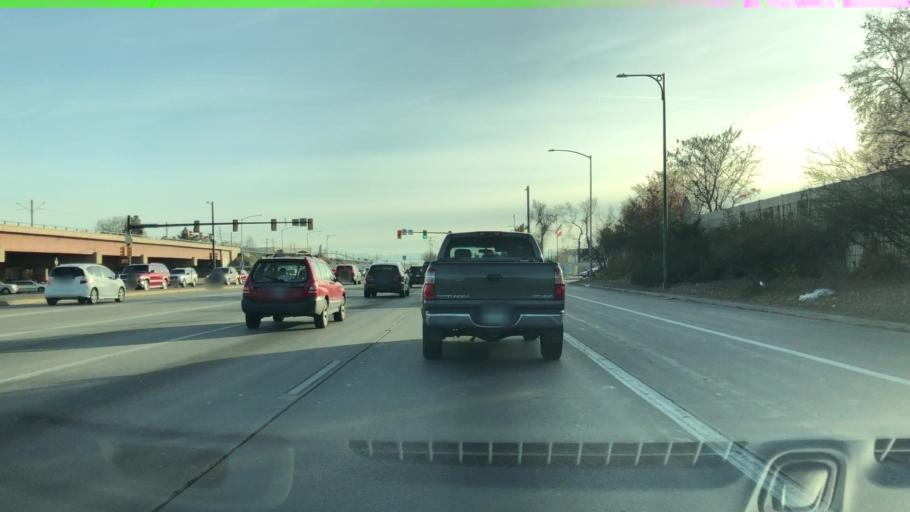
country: US
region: Colorado
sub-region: Arapahoe County
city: Englewood
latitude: 39.6614
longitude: -104.9985
